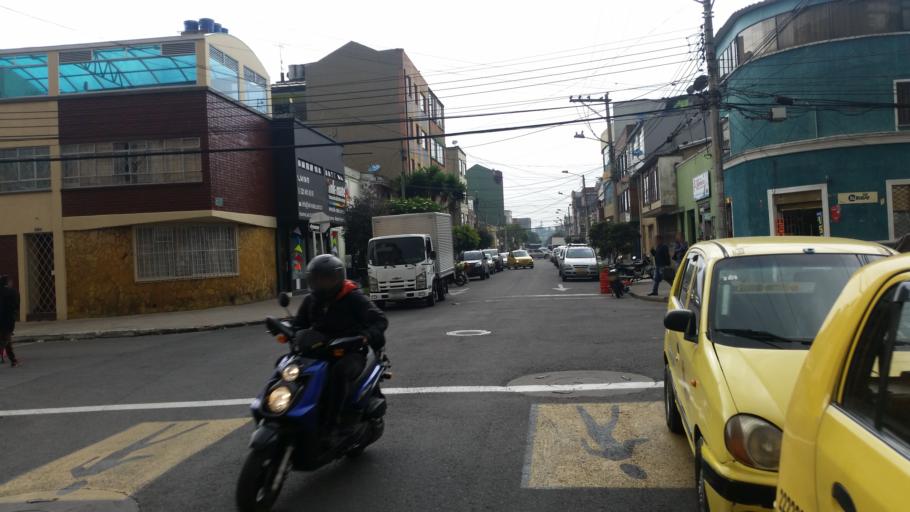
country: CO
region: Bogota D.C.
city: Bogota
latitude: 4.6522
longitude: -74.0732
